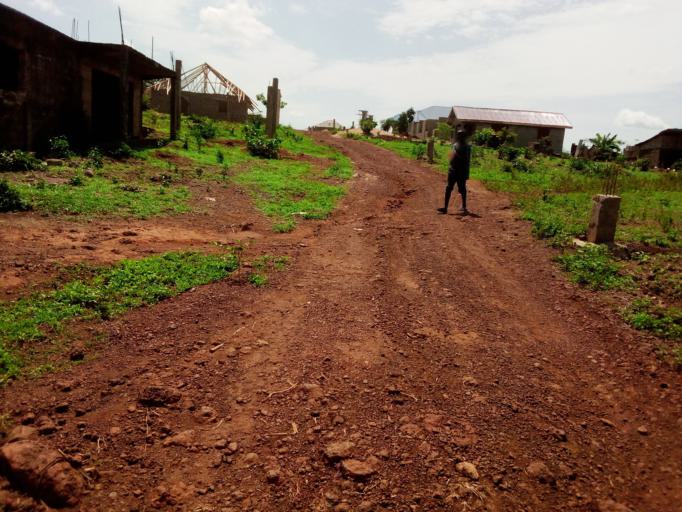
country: SL
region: Western Area
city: Waterloo
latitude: 8.3507
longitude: -13.0838
